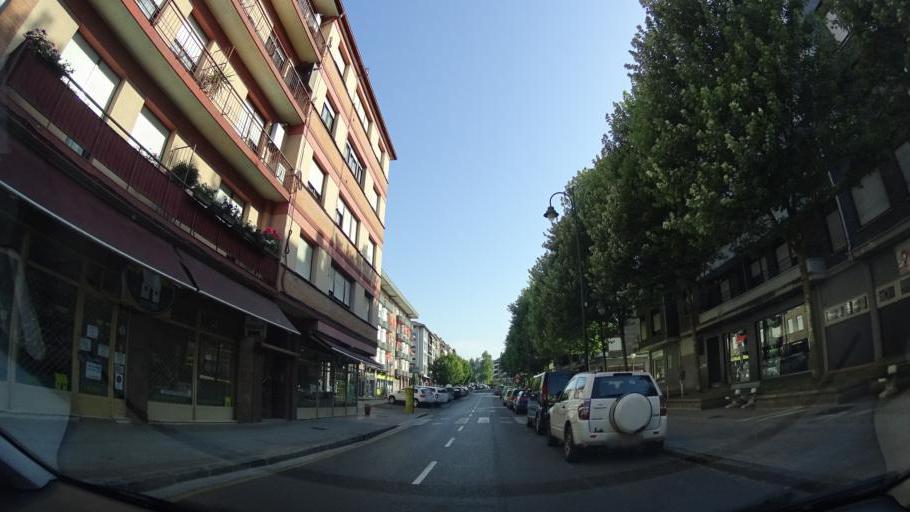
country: ES
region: Basque Country
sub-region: Bizkaia
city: Gernika-Lumo
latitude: 43.3076
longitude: -2.6806
